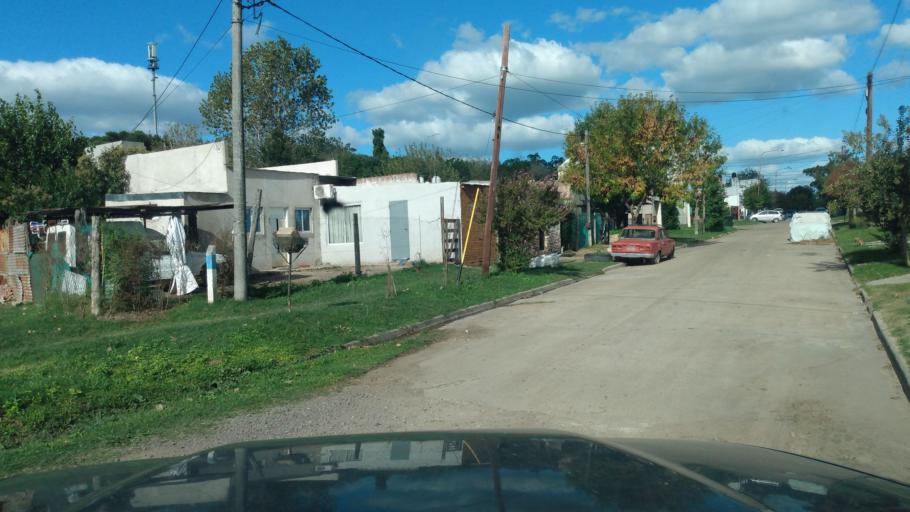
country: AR
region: Buenos Aires
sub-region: Partido de Lujan
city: Lujan
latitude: -34.5802
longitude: -59.1114
